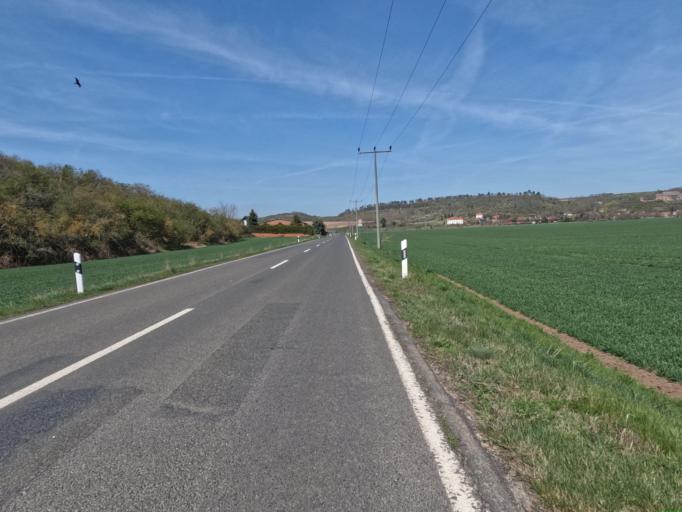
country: DE
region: Saxony-Anhalt
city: Beesenstedt
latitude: 51.6102
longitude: 11.7419
